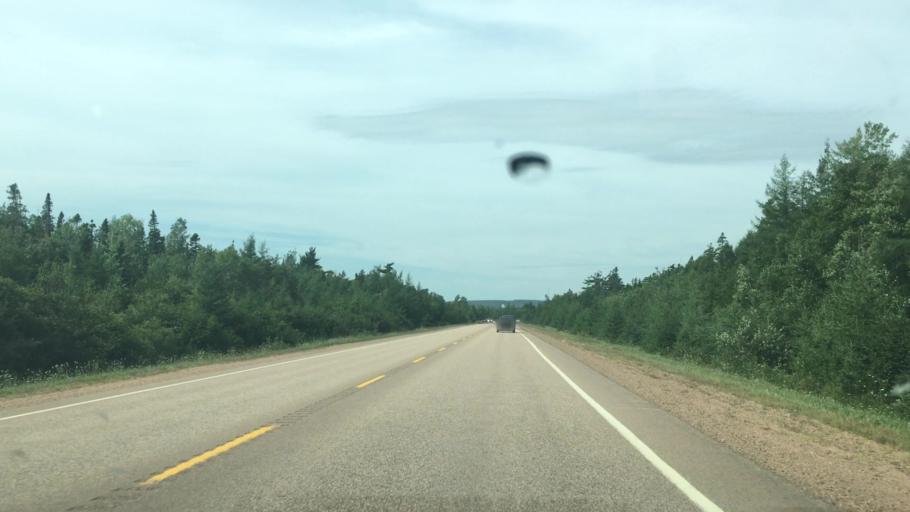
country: CA
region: Nova Scotia
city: Port Hawkesbury
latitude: 45.6047
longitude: -61.3071
